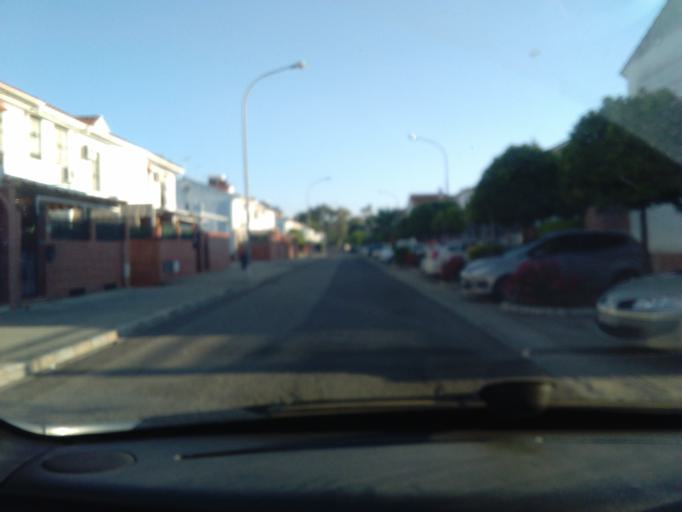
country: ES
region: Andalusia
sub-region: Provincia de Sevilla
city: Sevilla
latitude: 37.4103
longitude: -5.9369
